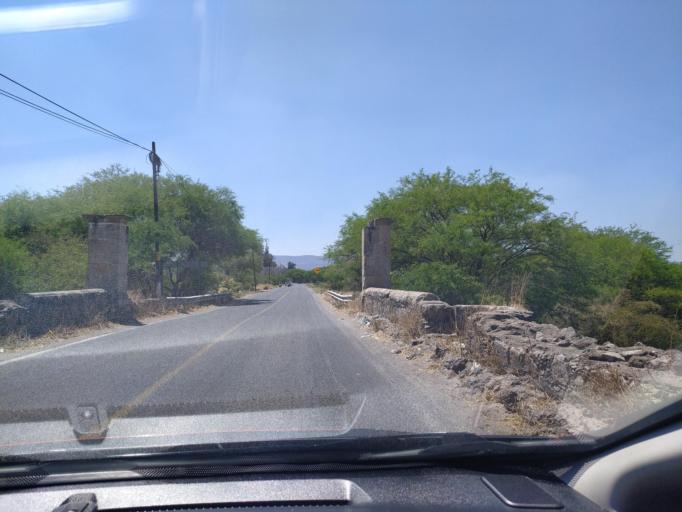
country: MX
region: Guanajuato
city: Ciudad Manuel Doblado
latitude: 20.7419
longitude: -101.9083
